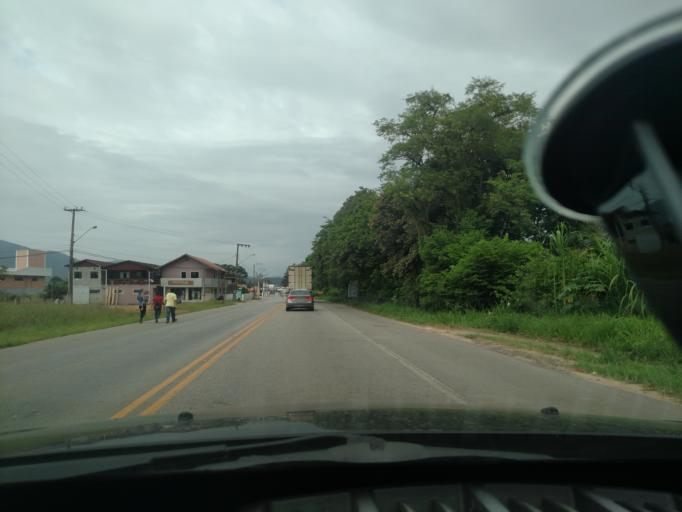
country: BR
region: Santa Catarina
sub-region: Gaspar
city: Gaspar
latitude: -26.8949
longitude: -48.8235
